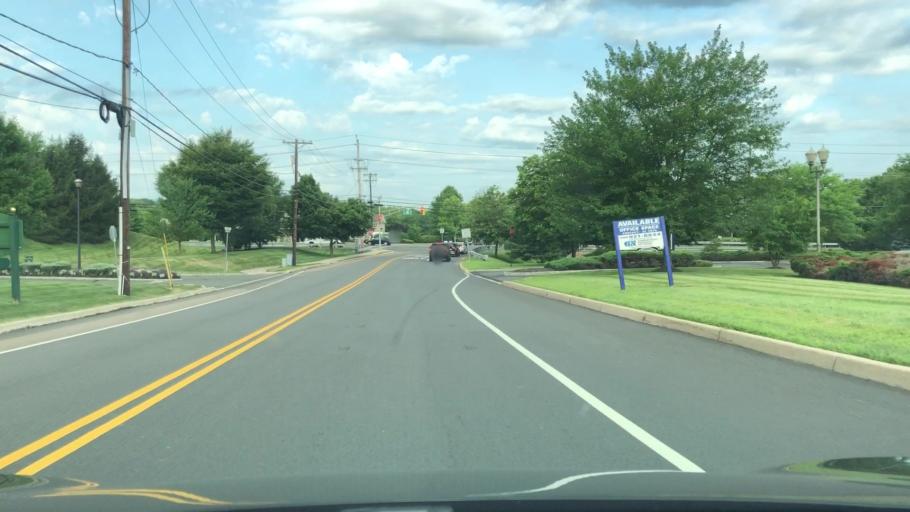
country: US
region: New Jersey
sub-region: Mercer County
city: Pennington
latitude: 40.3368
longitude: -74.7960
